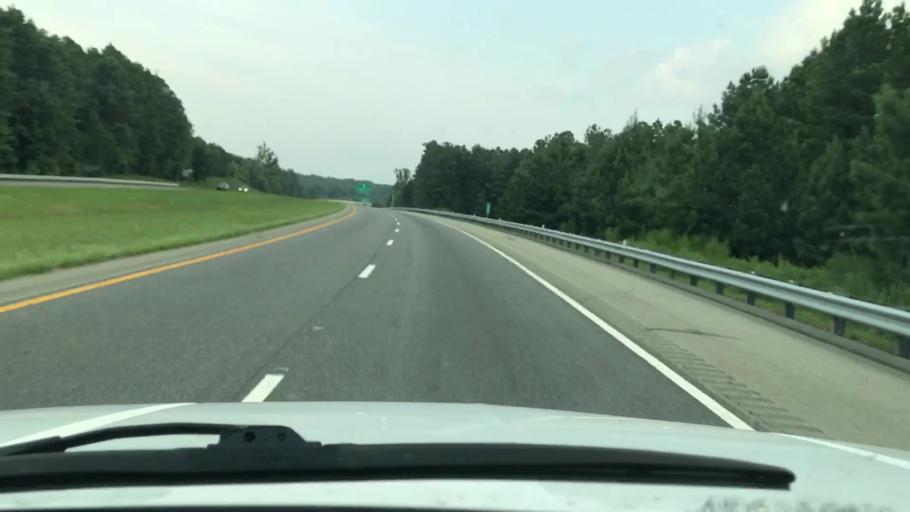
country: US
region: Virginia
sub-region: Chesterfield County
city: Brandermill
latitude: 37.5447
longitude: -77.6938
